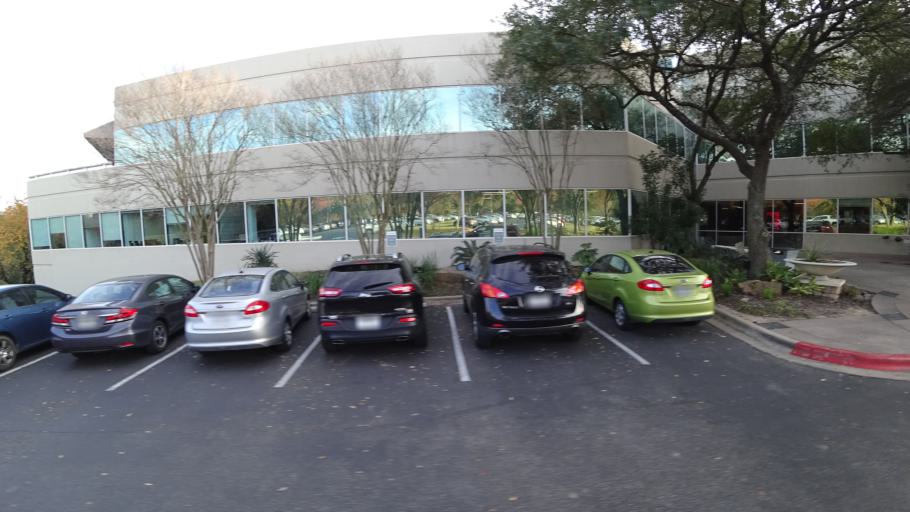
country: US
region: Texas
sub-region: Williamson County
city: Jollyville
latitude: 30.3893
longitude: -97.7565
